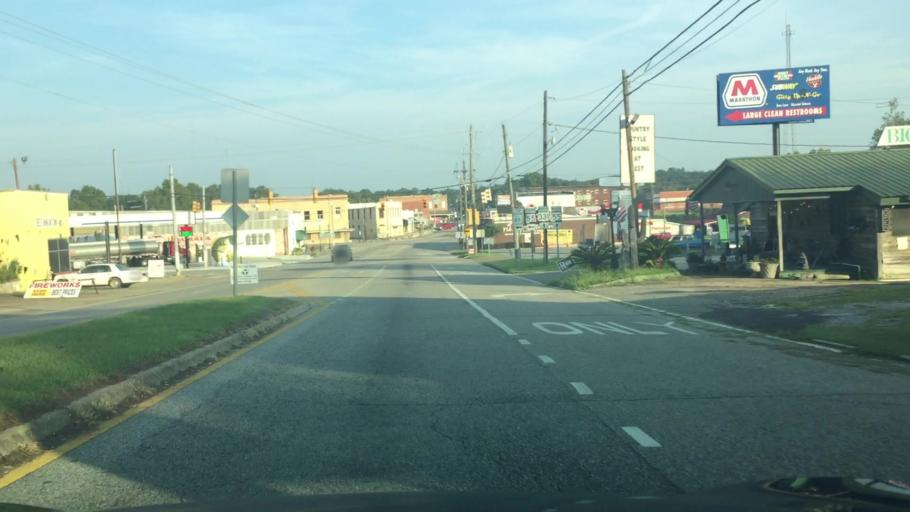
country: US
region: Alabama
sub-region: Covington County
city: Florala
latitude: 31.0042
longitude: -86.3259
